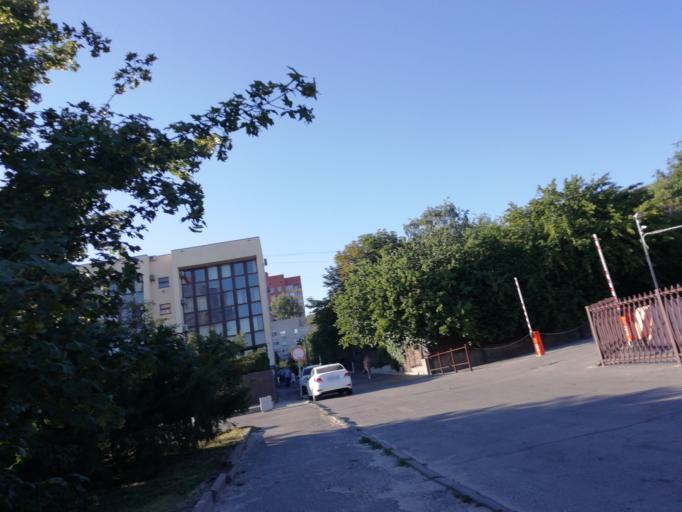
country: RU
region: Rostov
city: Severnyy
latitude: 47.2887
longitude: 39.7105
